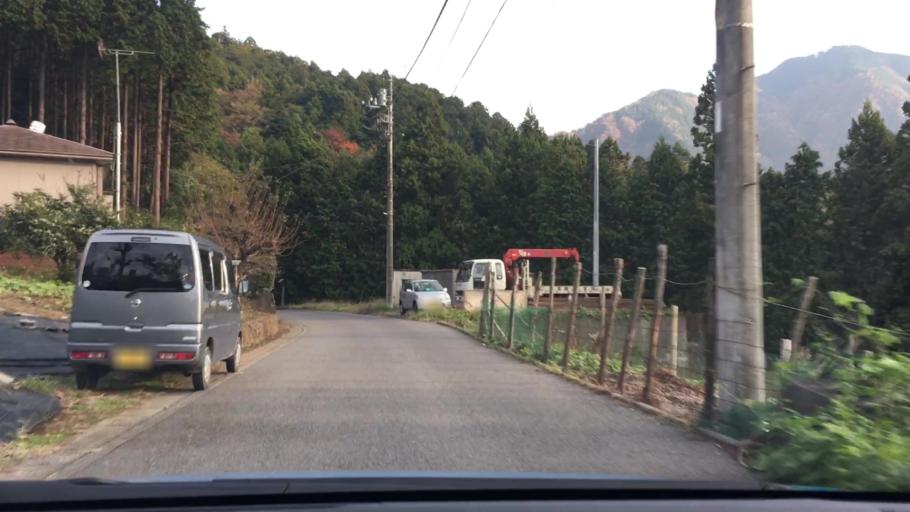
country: JP
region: Yamanashi
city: Uenohara
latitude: 35.5610
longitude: 139.1529
